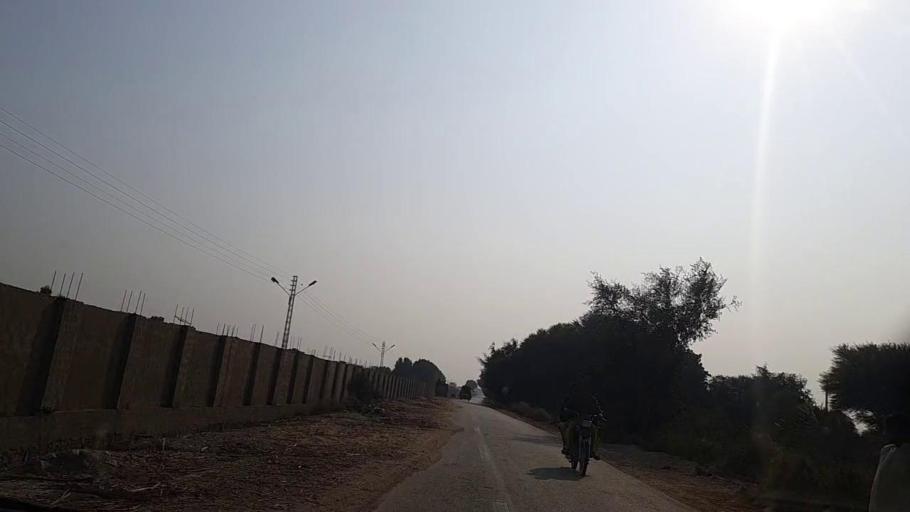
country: PK
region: Sindh
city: Sann
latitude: 26.1823
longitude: 68.1096
